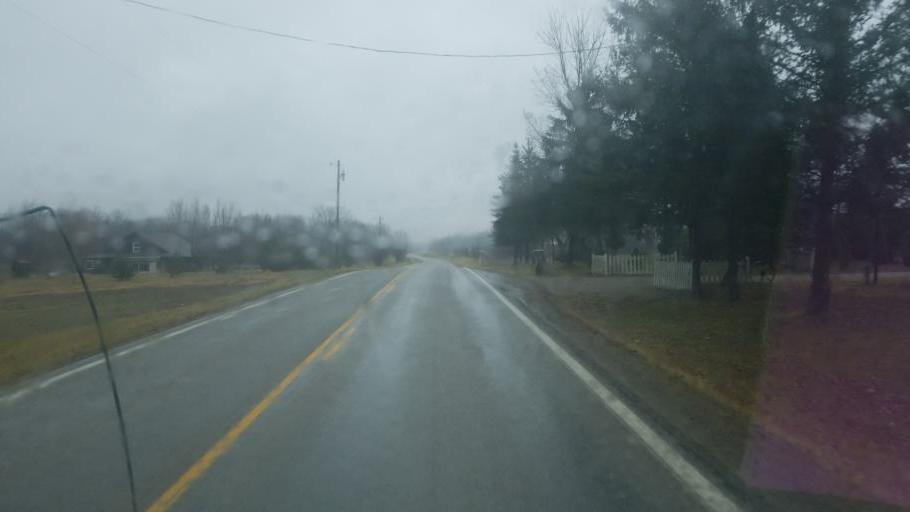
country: US
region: Ohio
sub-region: Crawford County
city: Galion
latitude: 40.6359
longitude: -82.7657
